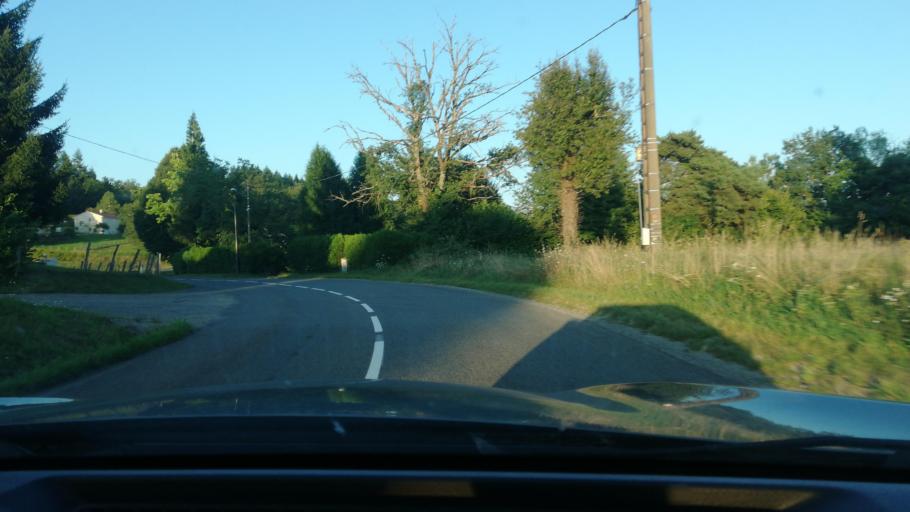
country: FR
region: Midi-Pyrenees
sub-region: Departement du Lot
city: Saint-Cere
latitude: 44.8765
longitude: 2.0240
